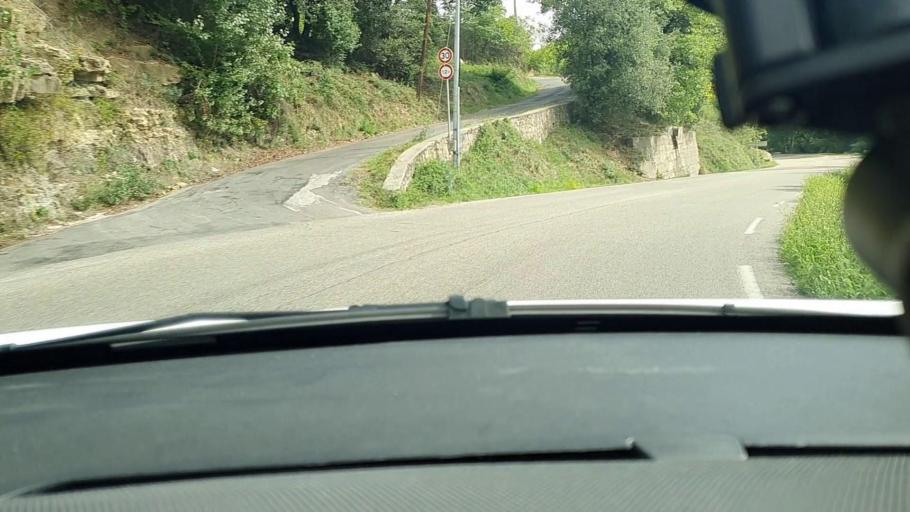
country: FR
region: Languedoc-Roussillon
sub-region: Departement du Gard
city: Branoux-les-Taillades
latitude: 44.2176
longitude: 4.0054
